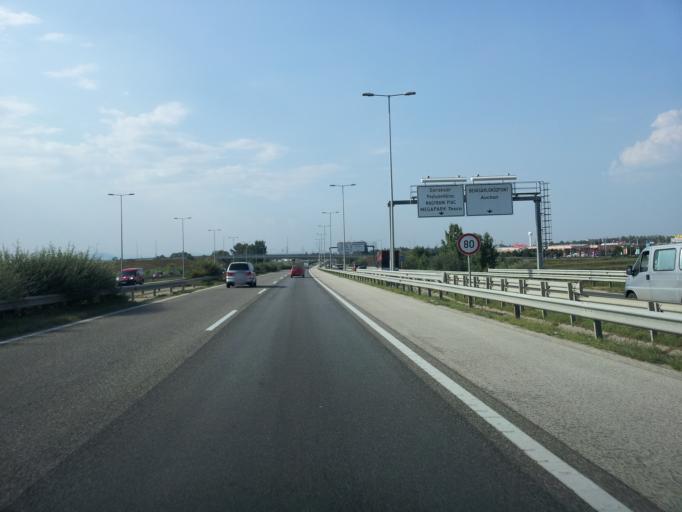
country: HU
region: Budapest
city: Budapest XVIII. keruelet
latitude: 47.4115
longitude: 19.1570
